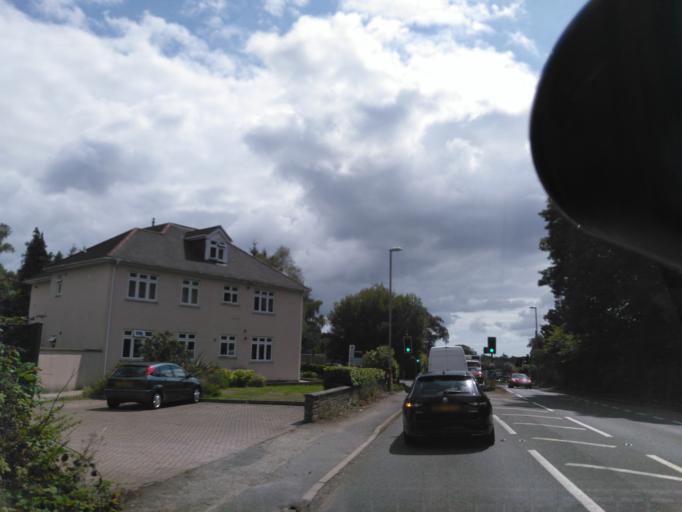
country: GB
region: England
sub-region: Dorset
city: Lytchett Matravers
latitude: 50.7521
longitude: -2.0443
